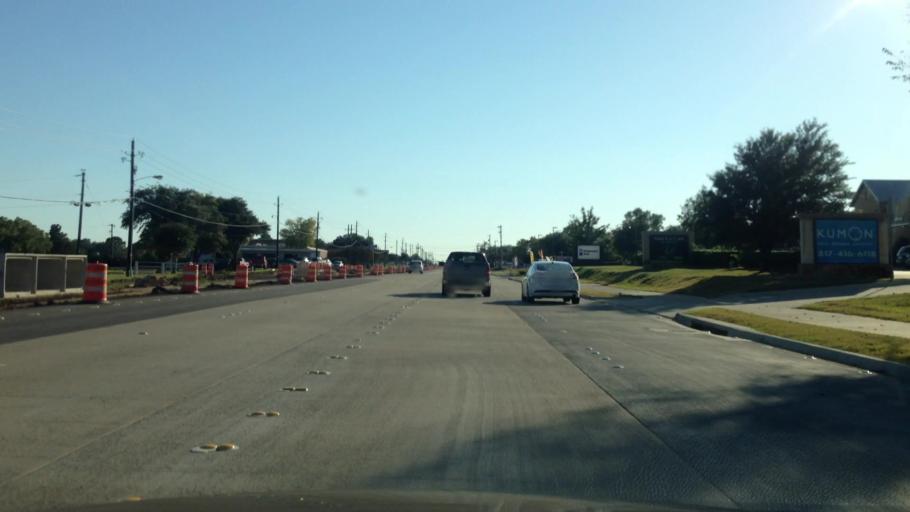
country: US
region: Texas
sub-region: Tarrant County
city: Colleyville
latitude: 32.8983
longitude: -97.1440
